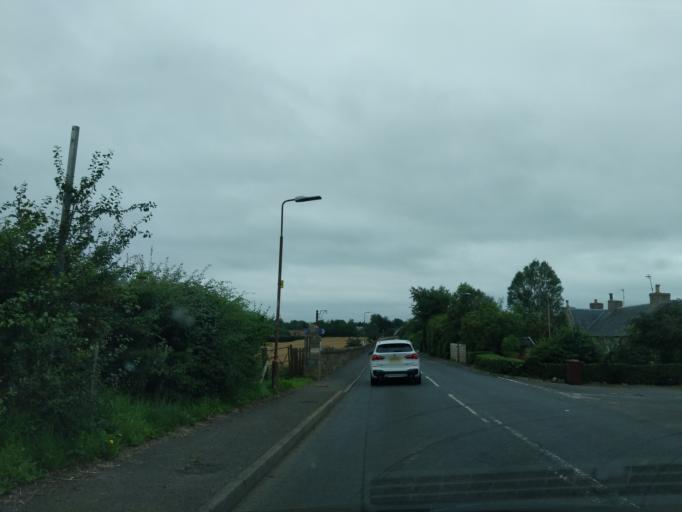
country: GB
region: Scotland
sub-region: East Lothian
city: Pencaitland
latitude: 55.9097
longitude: -2.9029
